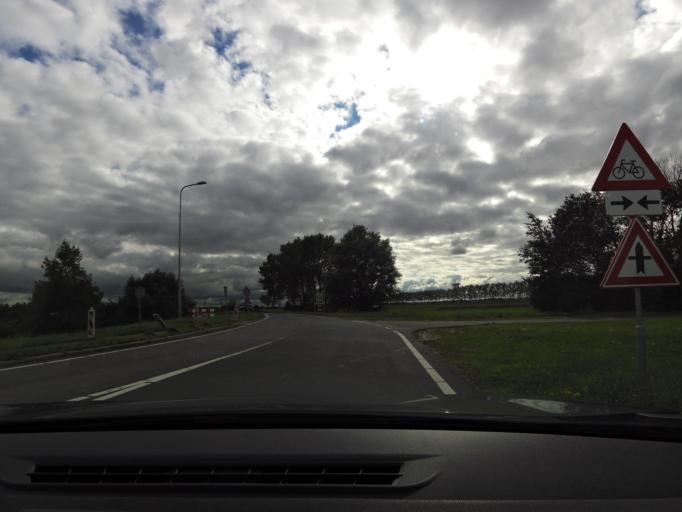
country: NL
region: South Holland
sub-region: Gemeente Brielle
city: Brielle
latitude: 51.8887
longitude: 4.2000
